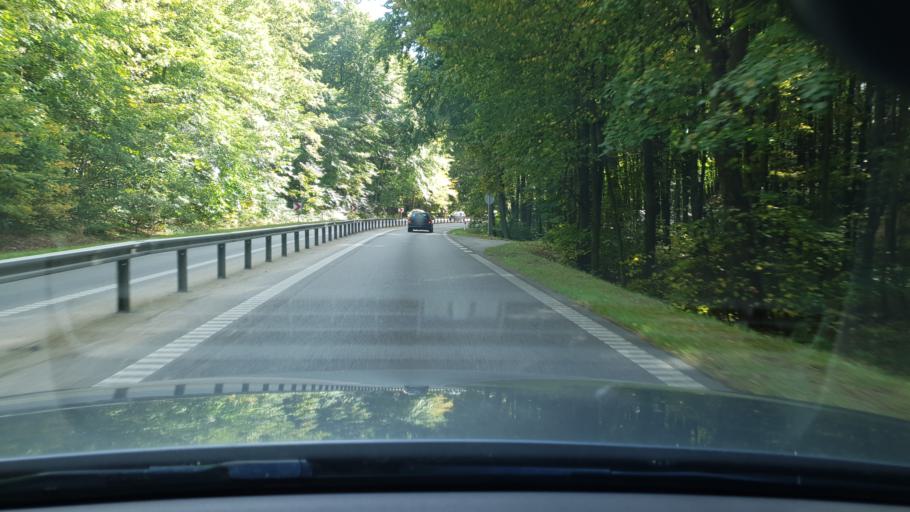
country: PL
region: Pomeranian Voivodeship
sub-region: Powiat wejherowski
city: Rekowo Dolne
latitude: 54.6306
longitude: 18.3443
